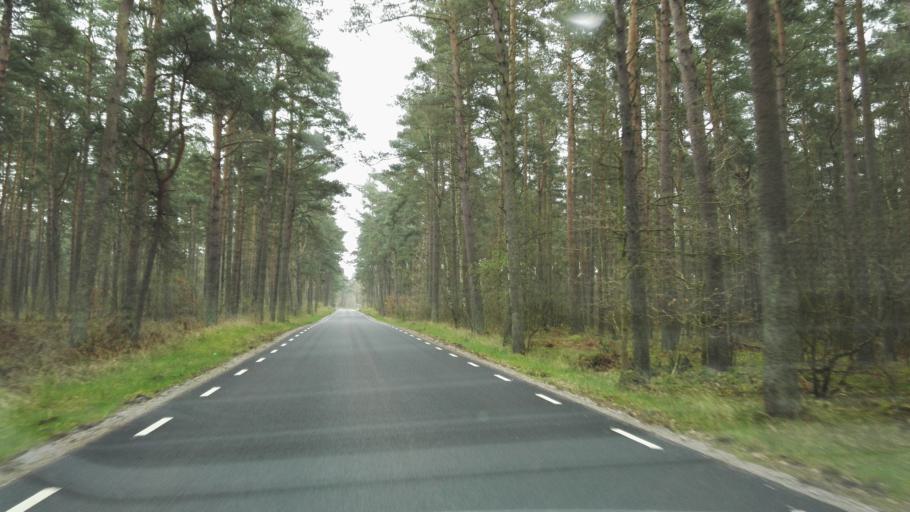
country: SE
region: Skane
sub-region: Simrishamns Kommun
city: Simrishamn
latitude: 55.3920
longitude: 14.1843
